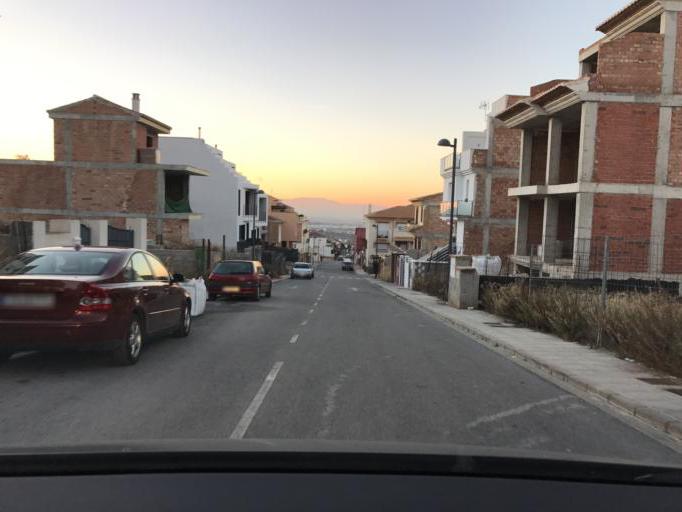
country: ES
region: Andalusia
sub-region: Provincia de Granada
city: Zubia
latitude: 37.1118
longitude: -3.5816
